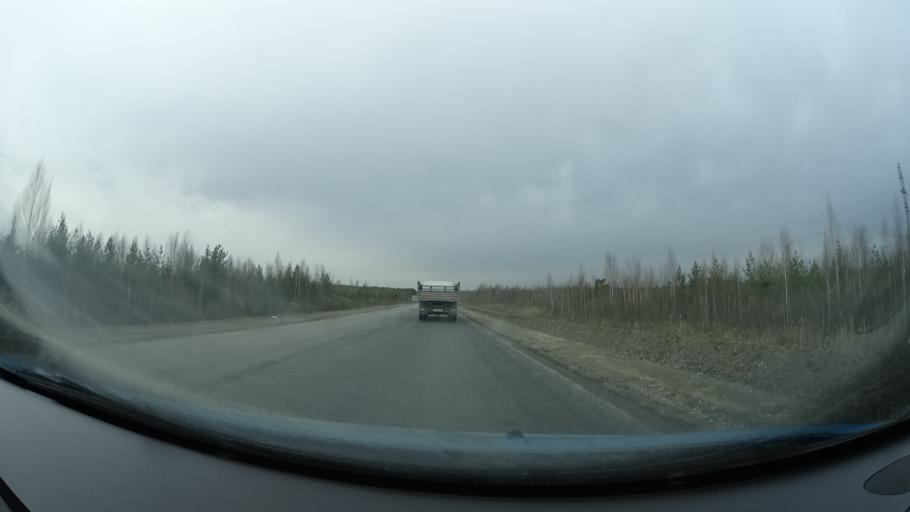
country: RU
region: Perm
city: Ust'-Kachka
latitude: 58.0854
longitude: 55.6715
